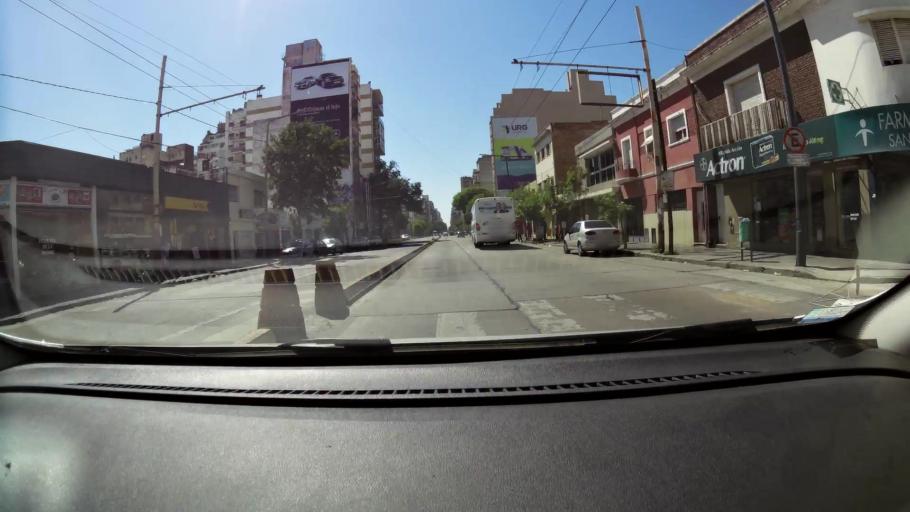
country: AR
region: Cordoba
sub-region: Departamento de Capital
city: Cordoba
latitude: -31.4081
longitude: -64.2020
